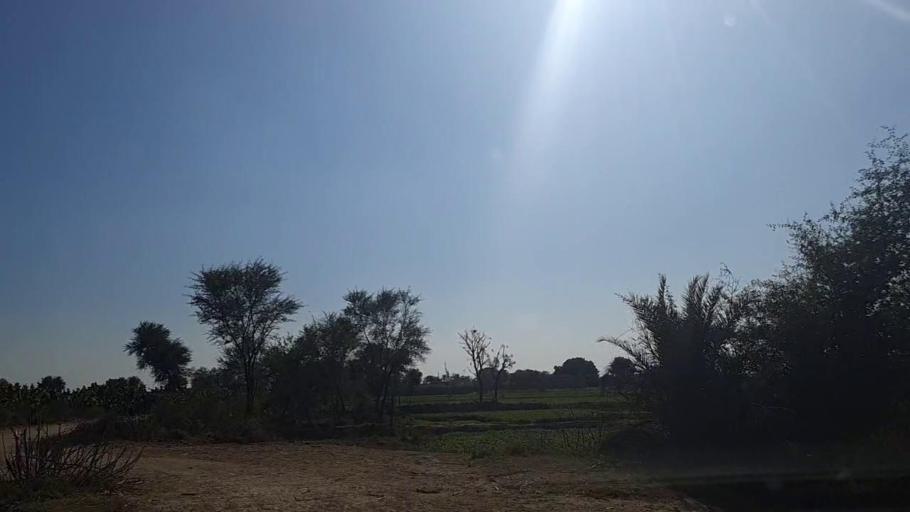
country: PK
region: Sindh
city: Sakrand
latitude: 26.2367
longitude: 68.1997
